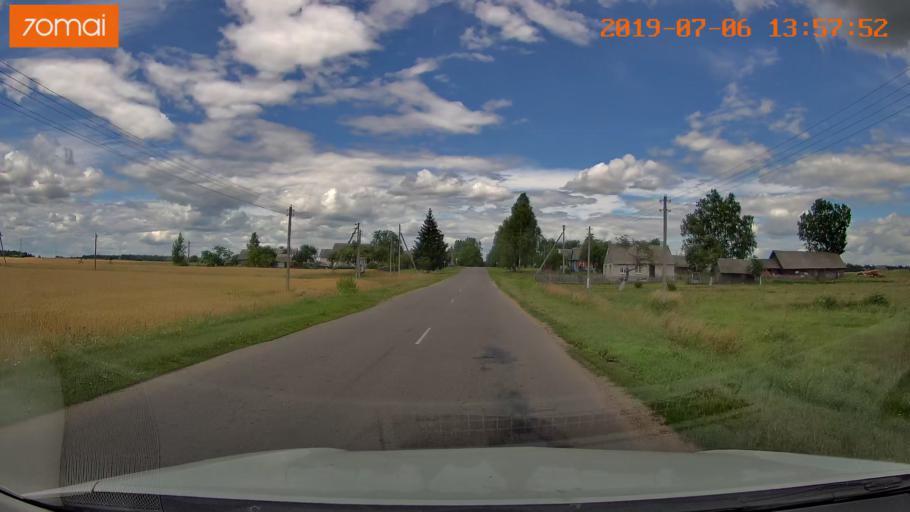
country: BY
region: Minsk
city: Ivyanyets
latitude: 53.7781
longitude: 26.8073
